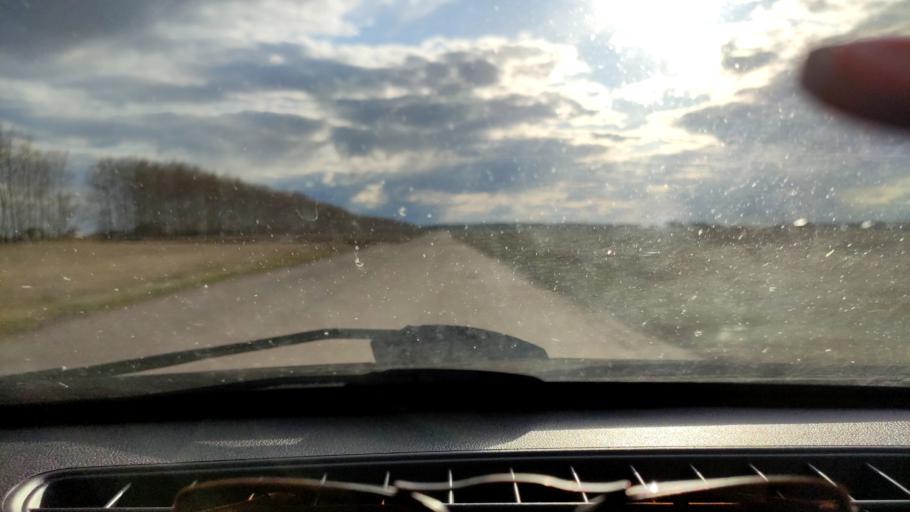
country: RU
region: Bashkortostan
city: Karmaskaly
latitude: 54.3508
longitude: 56.1285
